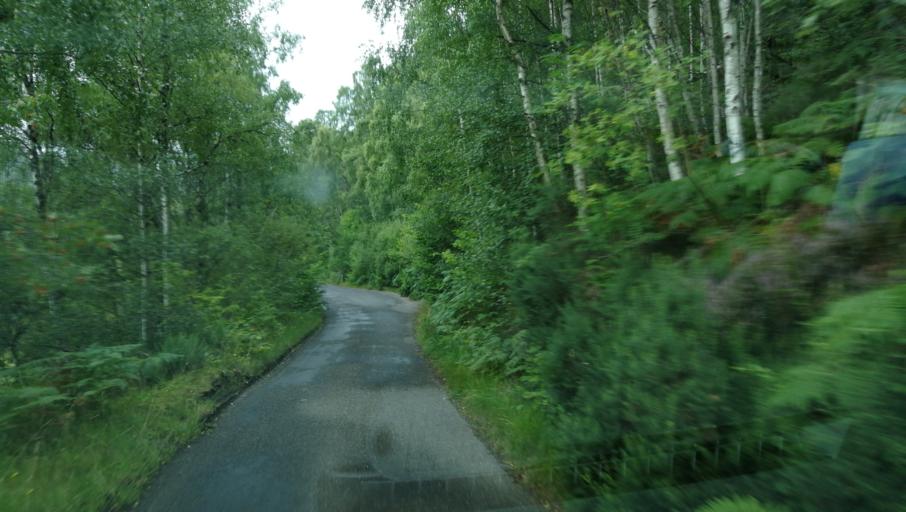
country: GB
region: Scotland
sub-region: Highland
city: Beauly
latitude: 57.3172
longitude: -4.8291
